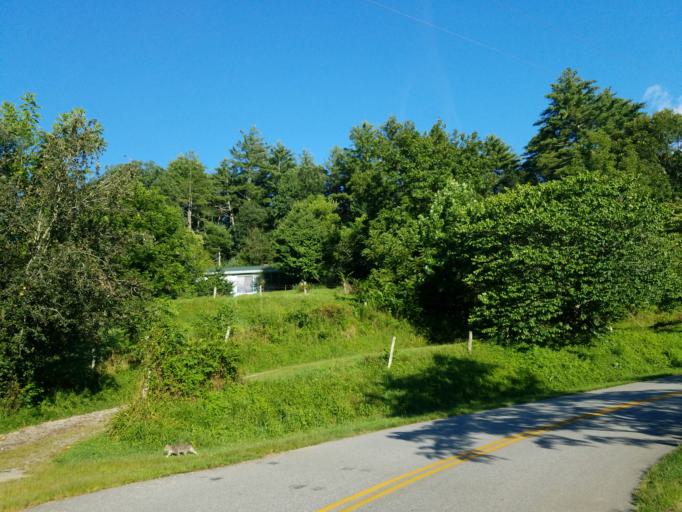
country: US
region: Georgia
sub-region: Union County
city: Blairsville
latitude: 34.7642
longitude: -84.1011
